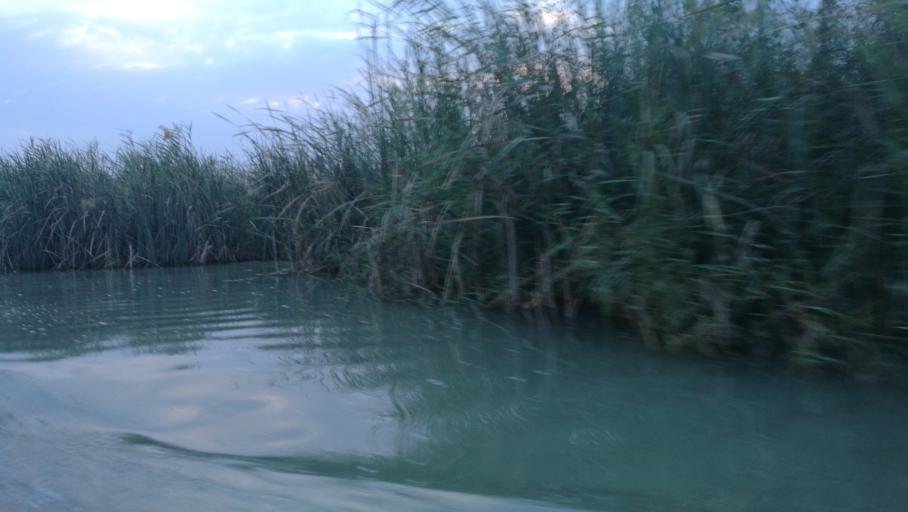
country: IQ
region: Dhi Qar
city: Al Jabayish
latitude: 30.9838
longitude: 47.0370
